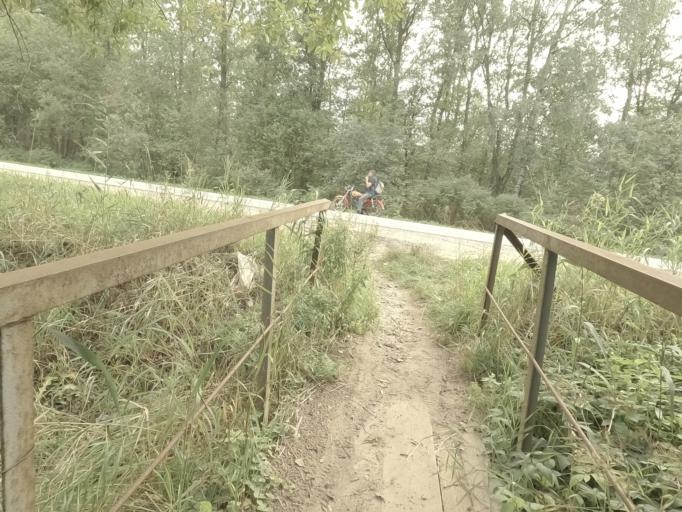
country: RU
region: Leningrad
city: Mga
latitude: 59.7628
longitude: 30.9892
